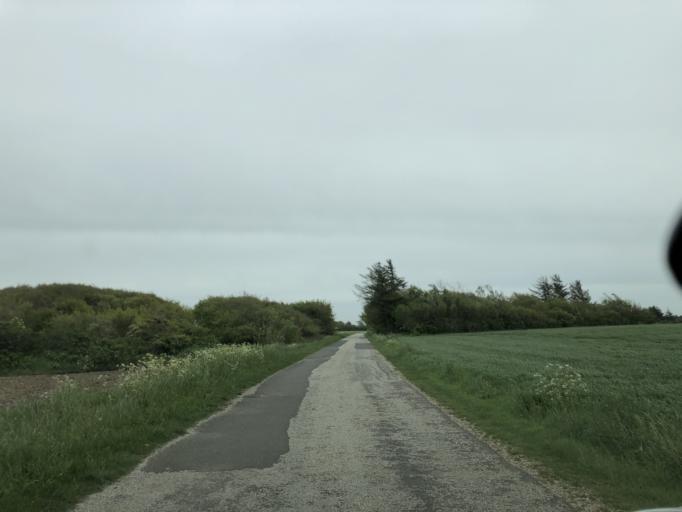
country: DK
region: Central Jutland
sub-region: Holstebro Kommune
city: Ulfborg
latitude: 56.2731
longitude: 8.1790
